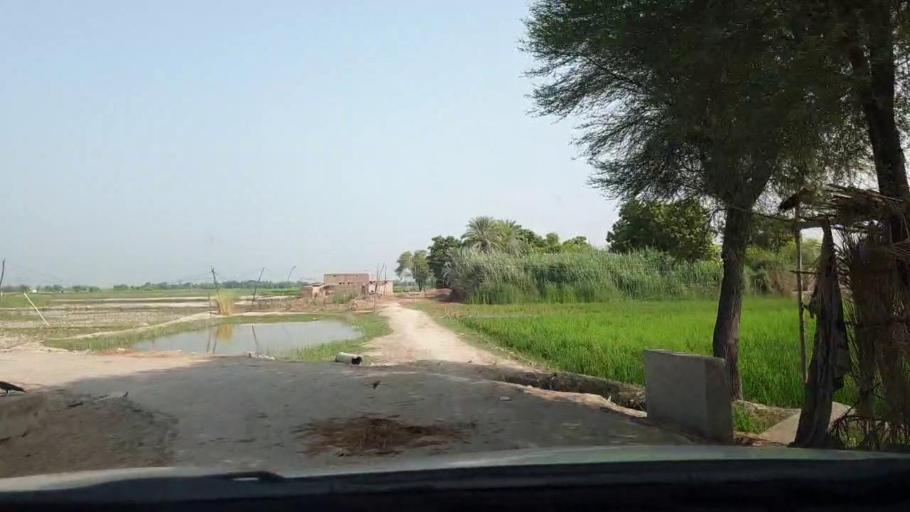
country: PK
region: Sindh
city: Goth Garelo
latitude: 27.4583
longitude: 68.1219
